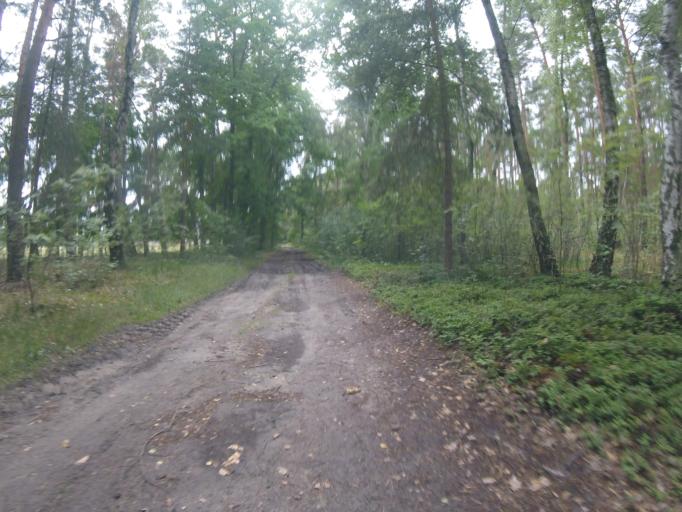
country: DE
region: Brandenburg
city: Bestensee
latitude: 52.2594
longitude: 13.7046
